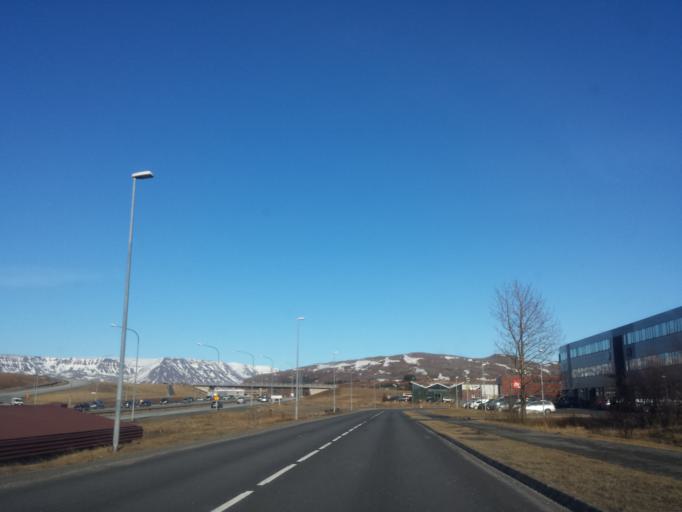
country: IS
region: Capital Region
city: Mosfellsbaer
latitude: 64.1295
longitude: -21.7684
